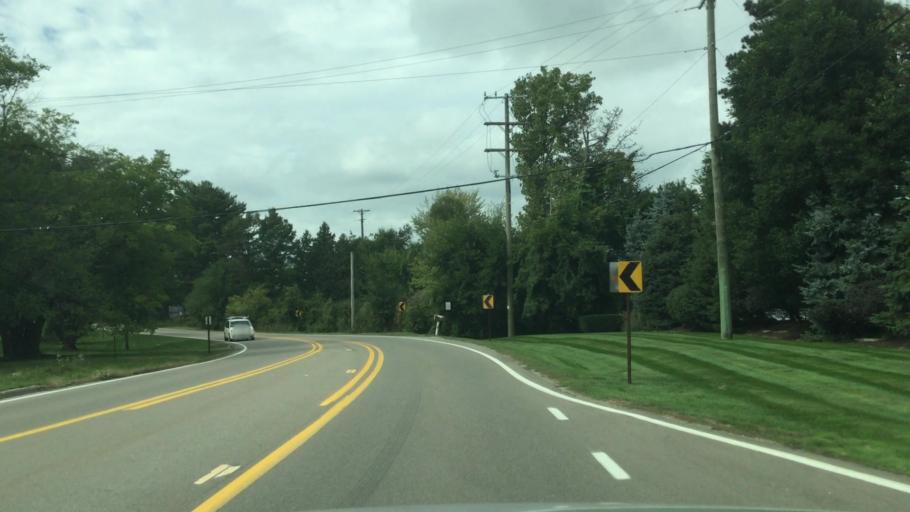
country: US
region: Michigan
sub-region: Livingston County
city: Brighton
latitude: 42.5518
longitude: -83.7709
